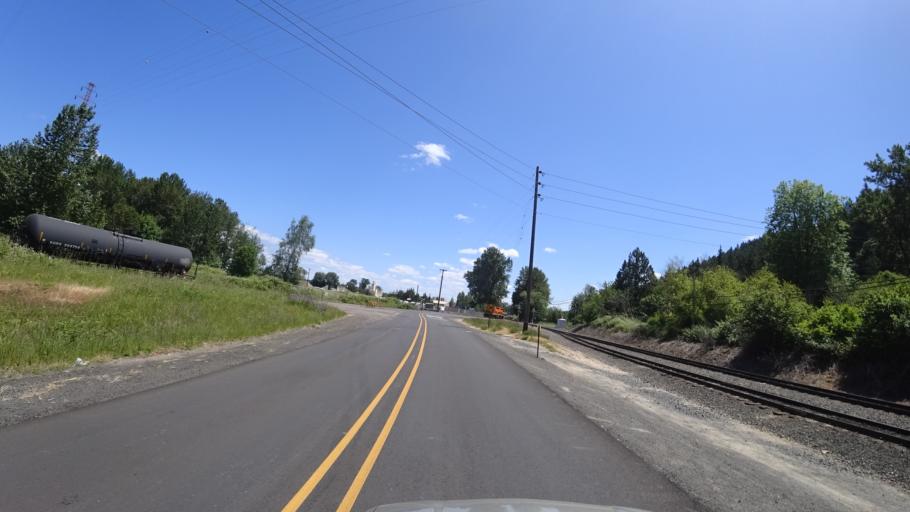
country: US
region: Oregon
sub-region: Washington County
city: Oak Hills
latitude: 45.6121
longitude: -122.7965
